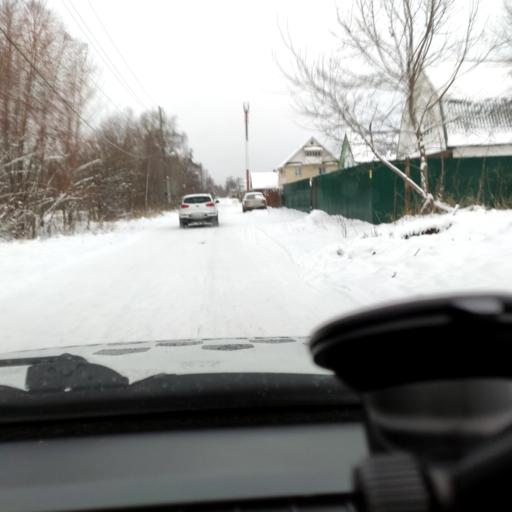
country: RU
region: Perm
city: Perm
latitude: 58.0573
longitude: 56.3621
